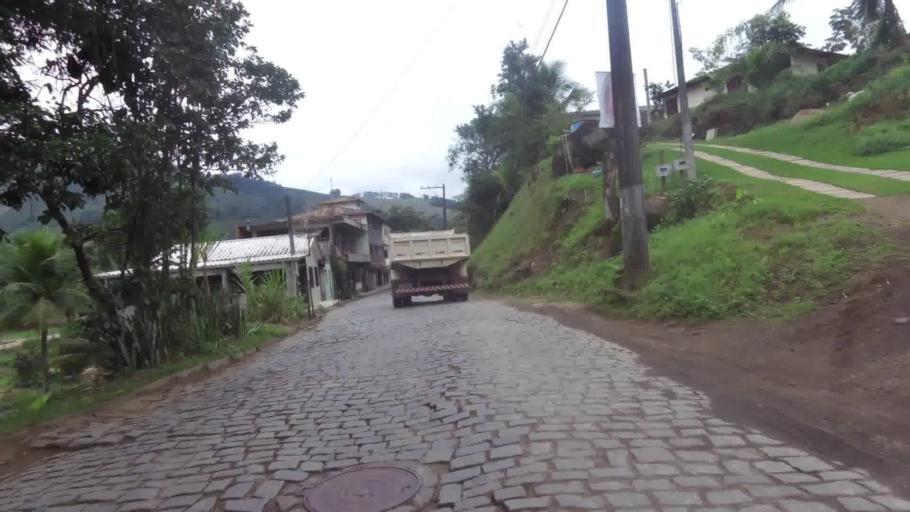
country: BR
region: Espirito Santo
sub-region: Iconha
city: Iconha
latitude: -20.7678
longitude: -40.8329
